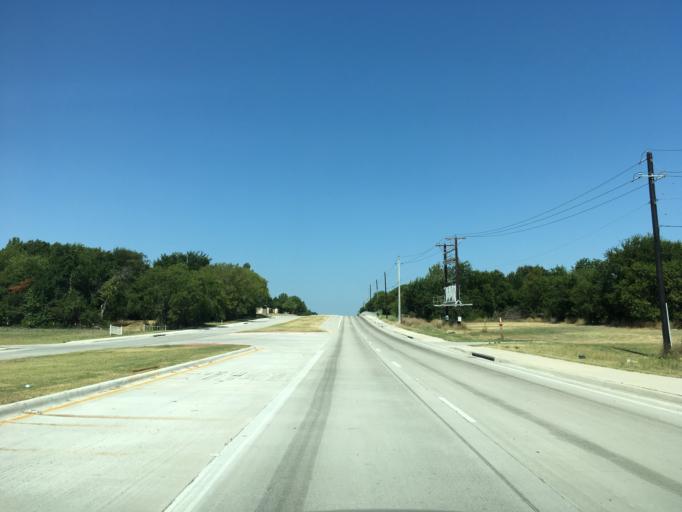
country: US
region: Texas
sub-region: Collin County
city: Fairview
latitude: 33.1288
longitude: -96.6146
